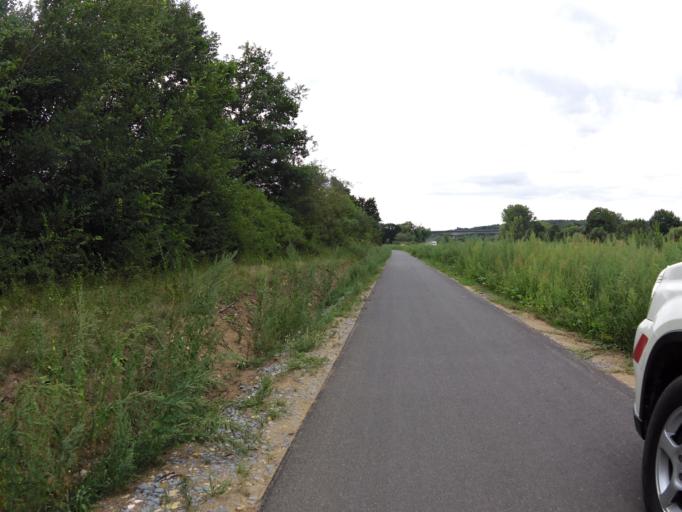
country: DE
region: Bavaria
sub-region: Regierungsbezirk Unterfranken
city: Schonungen
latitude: 50.0303
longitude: 10.3219
